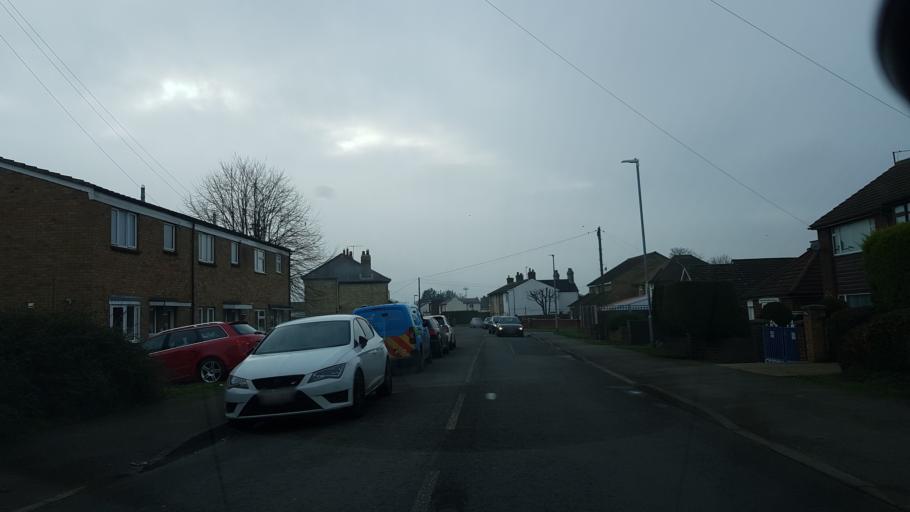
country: GB
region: England
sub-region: Central Bedfordshire
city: Biggleswade
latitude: 52.0932
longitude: -0.2565
